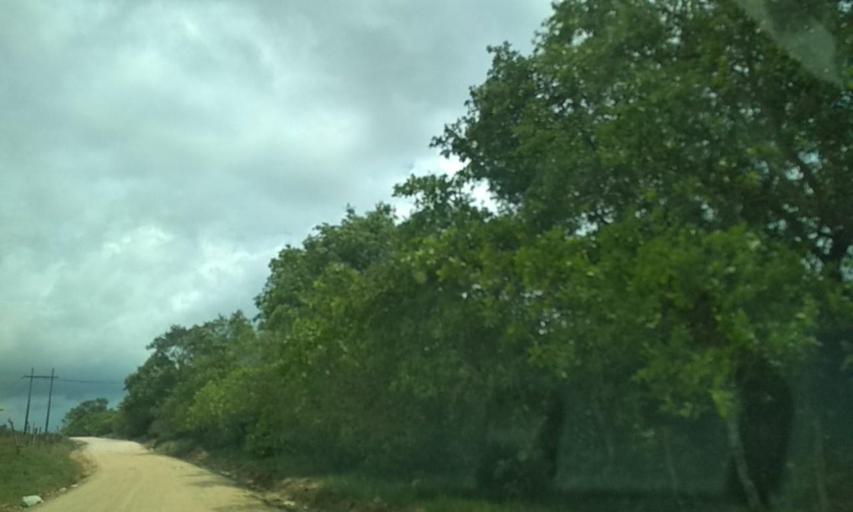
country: MX
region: Veracruz
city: Las Choapas
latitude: 17.9054
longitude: -94.1253
